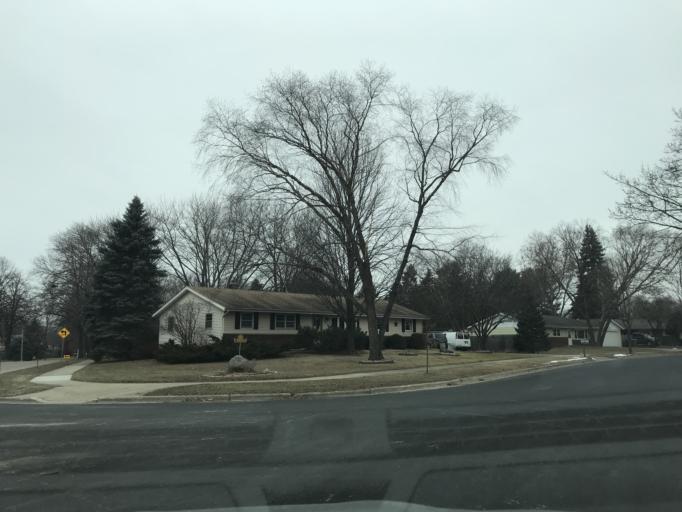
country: US
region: Wisconsin
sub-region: Dane County
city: Monona
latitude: 43.0973
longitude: -89.2888
